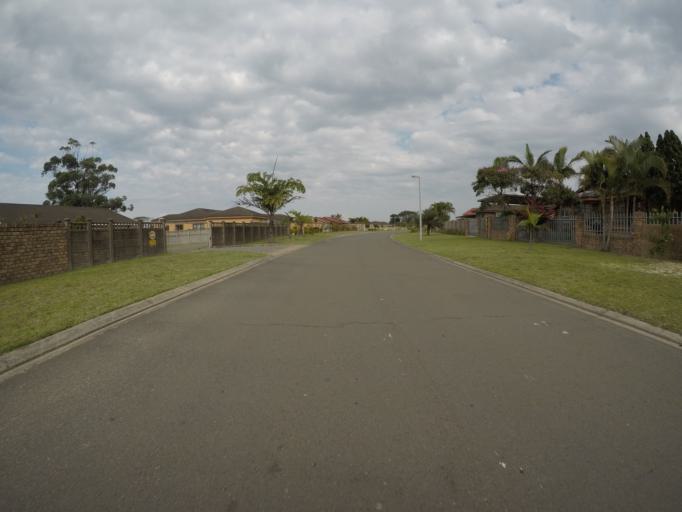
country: ZA
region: KwaZulu-Natal
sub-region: uThungulu District Municipality
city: Richards Bay
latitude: -28.7343
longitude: 32.0902
